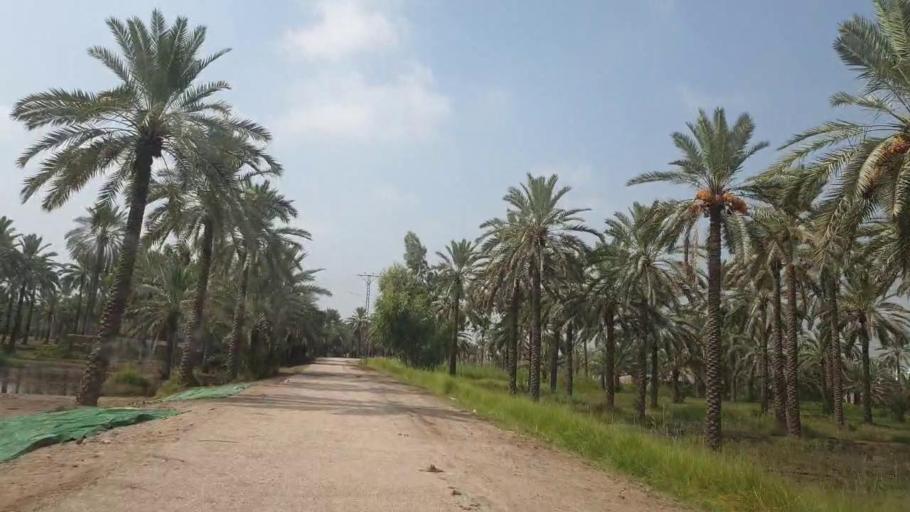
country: PK
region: Sindh
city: Khairpur
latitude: 27.5591
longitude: 68.7592
